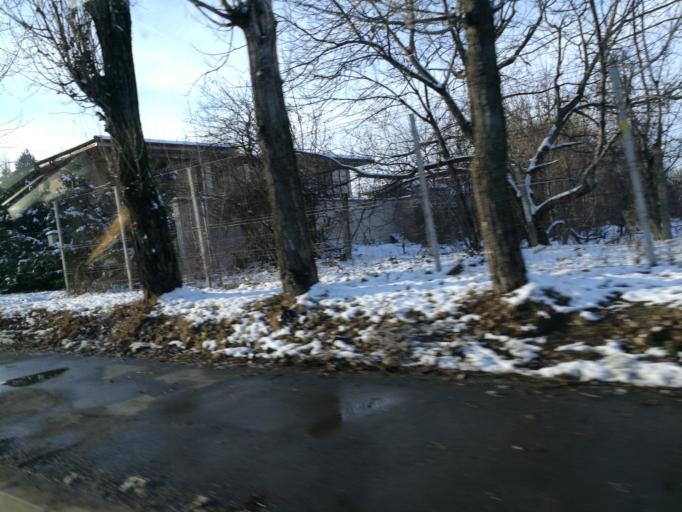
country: RO
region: Ilfov
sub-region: Comuna Otopeni
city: Otopeni
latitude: 44.4923
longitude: 26.0596
